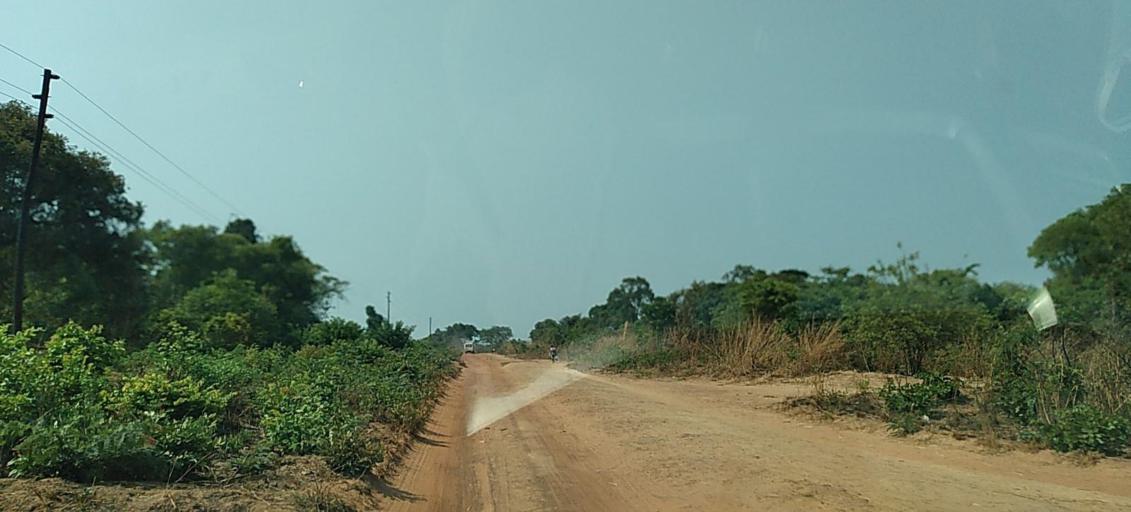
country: ZM
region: Copperbelt
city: Chingola
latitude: -12.9185
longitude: 27.3732
